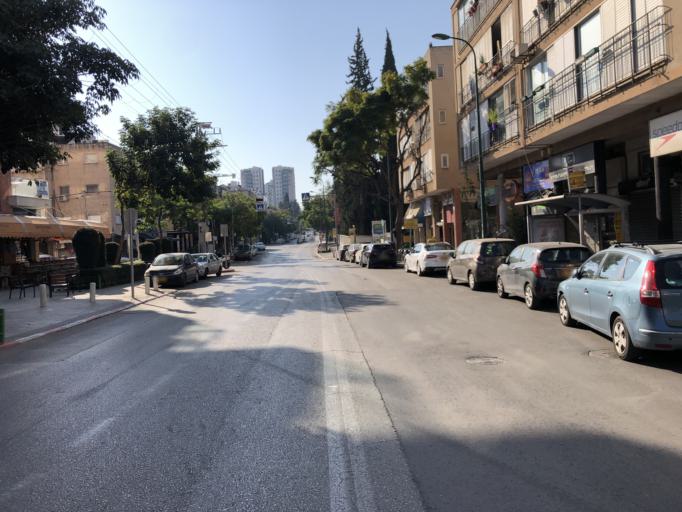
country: IL
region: Tel Aviv
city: Giv`atayim
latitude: 32.0734
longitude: 34.8086
